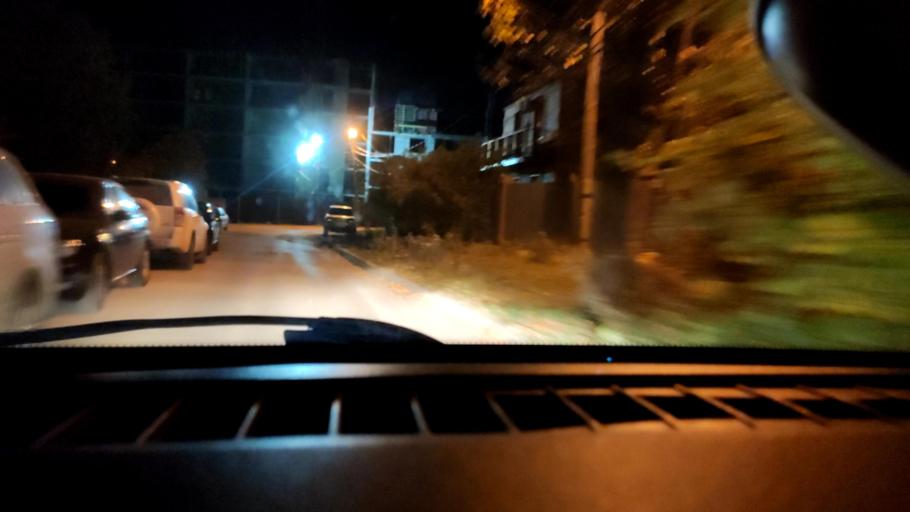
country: RU
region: Samara
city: Samara
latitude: 53.2235
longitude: 50.1543
